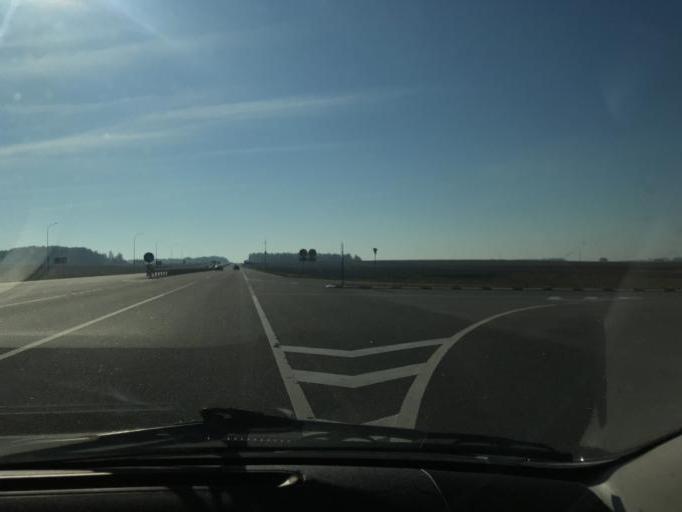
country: BY
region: Minsk
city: Slutsk
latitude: 53.2135
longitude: 27.5505
